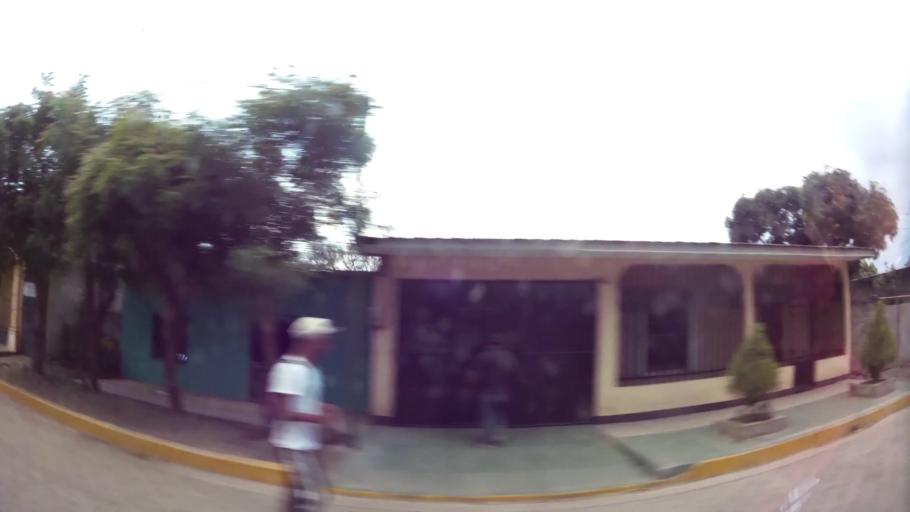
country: NI
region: Matagalpa
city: Ciudad Dario
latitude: 12.8513
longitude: -86.0943
